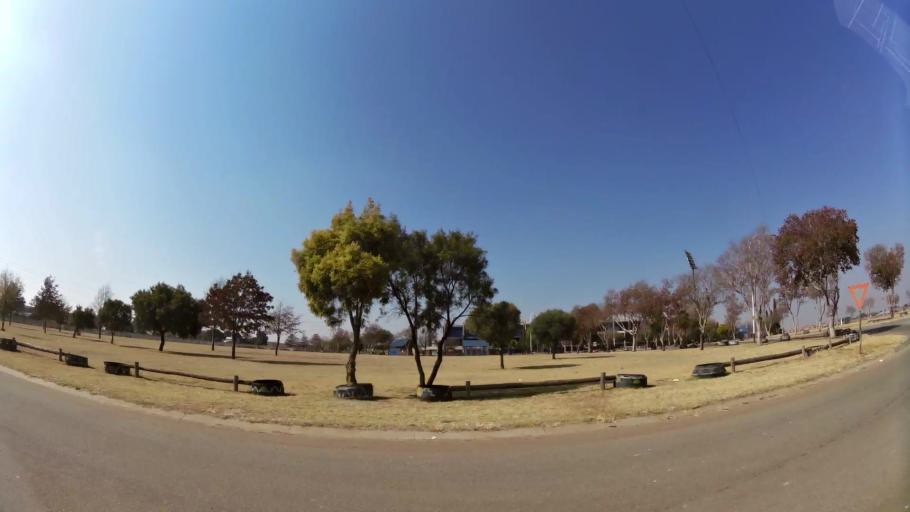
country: ZA
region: Gauteng
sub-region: Ekurhuleni Metropolitan Municipality
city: Boksburg
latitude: -26.2348
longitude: 28.2755
